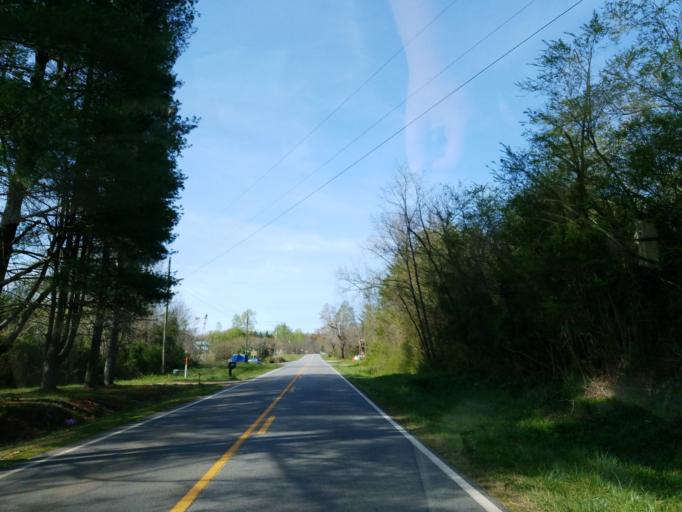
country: US
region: Georgia
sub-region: Lumpkin County
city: Dahlonega
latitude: 34.4734
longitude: -84.0237
